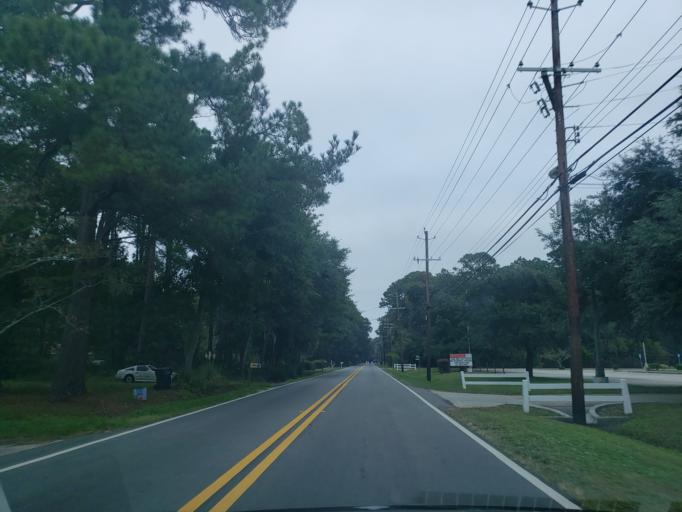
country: US
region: Georgia
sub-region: Chatham County
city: Montgomery
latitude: 31.9524
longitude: -81.1040
